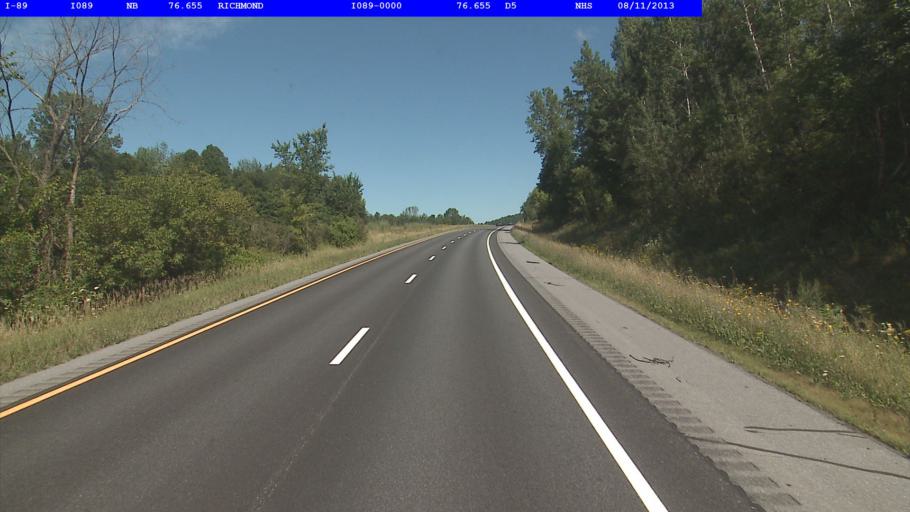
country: US
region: Vermont
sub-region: Chittenden County
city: Williston
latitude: 44.4058
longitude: -72.9893
